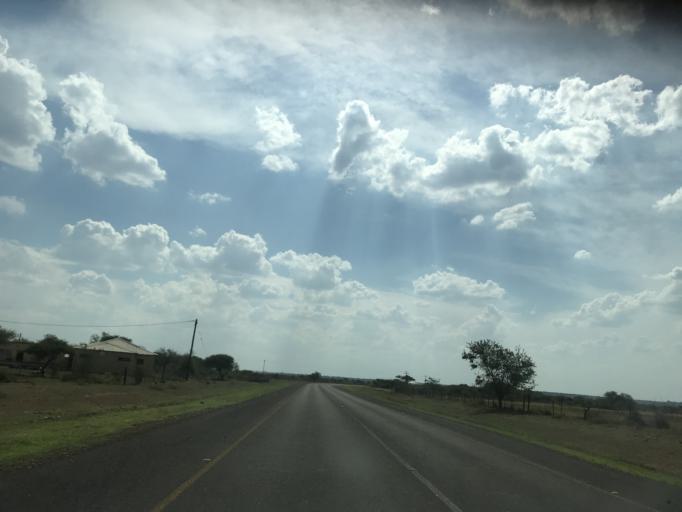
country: BW
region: South East
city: Janeng
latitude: -25.4939
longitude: 25.6372
